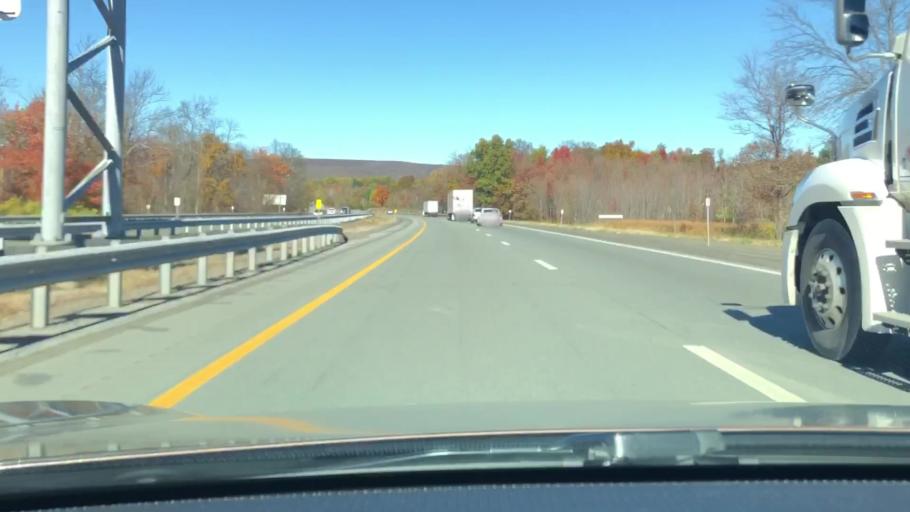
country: US
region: New York
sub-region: Orange County
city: Central Valley
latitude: 41.3268
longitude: -74.1128
